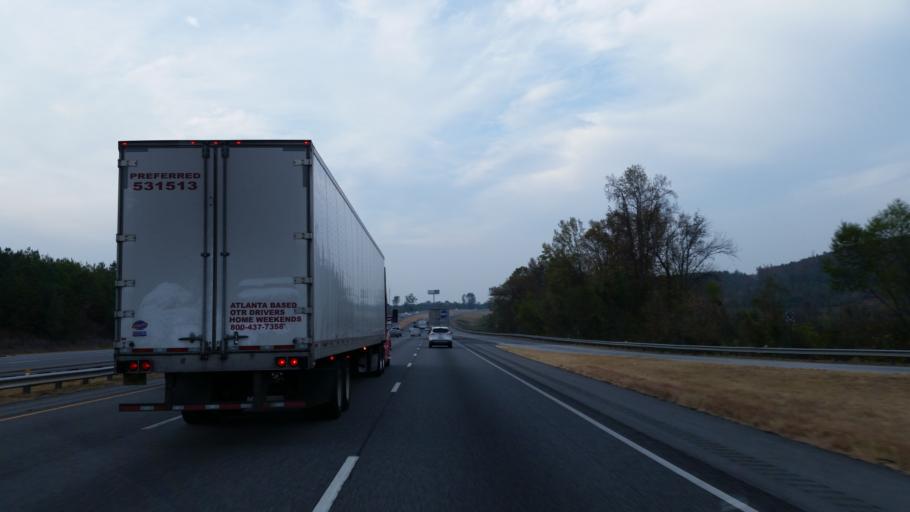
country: US
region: Georgia
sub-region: Bartow County
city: Adairsville
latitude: 34.3791
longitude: -84.9126
